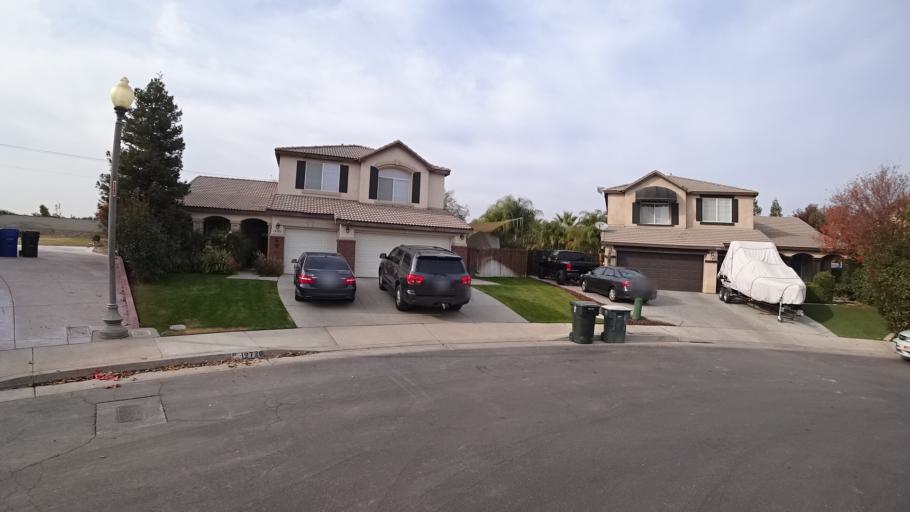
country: US
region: California
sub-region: Kern County
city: Rosedale
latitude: 35.3405
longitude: -119.1445
